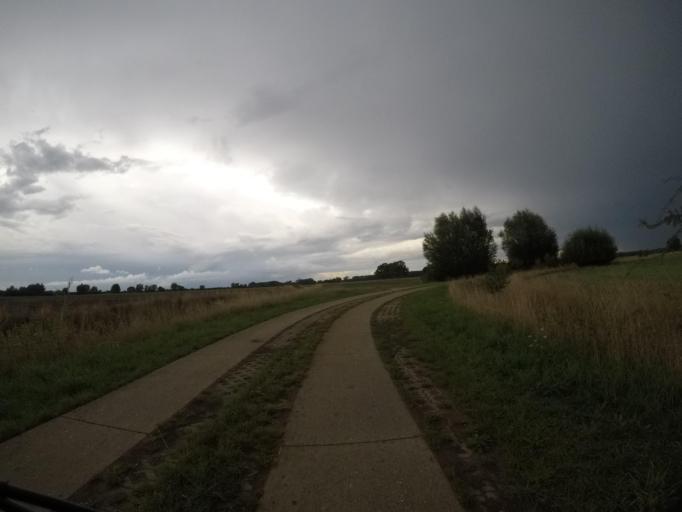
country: DE
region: Lower Saxony
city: Neu Darchau
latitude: 53.2572
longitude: 10.8869
